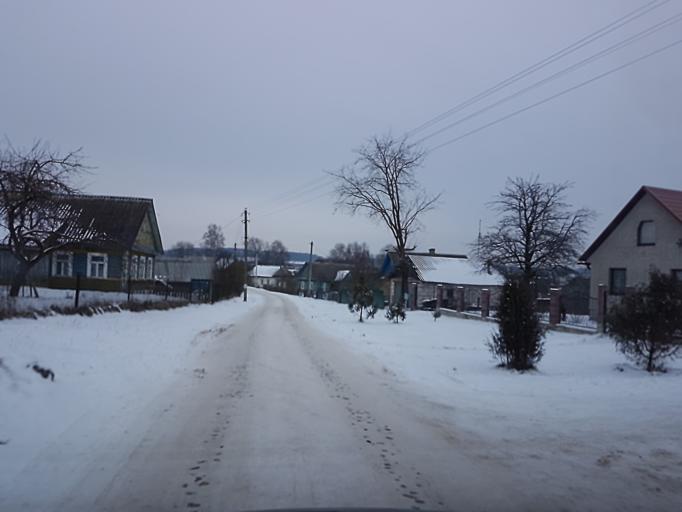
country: BY
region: Minsk
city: Rakaw
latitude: 53.9640
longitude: 27.0464
